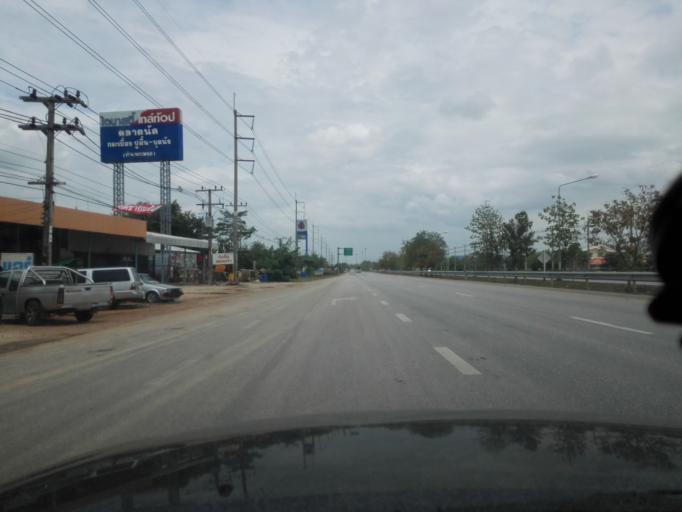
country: TH
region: Kamphaeng Phet
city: Kamphaeng Phet
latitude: 16.4884
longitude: 99.4856
